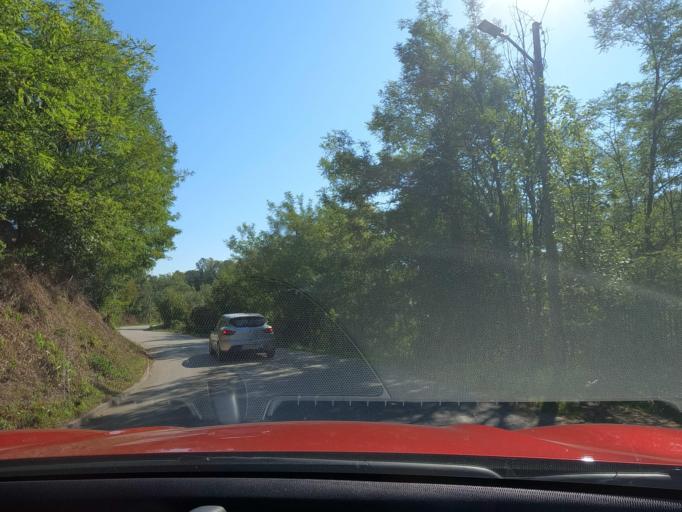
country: RS
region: Central Serbia
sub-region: Raski Okrug
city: Kraljevo
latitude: 43.7697
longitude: 20.6620
